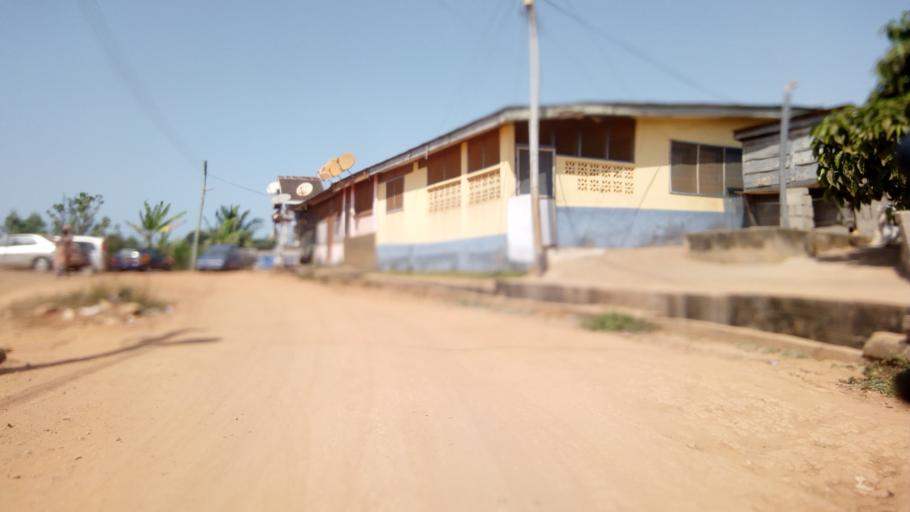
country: GH
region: Central
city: Cape Coast
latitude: 5.1125
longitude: -1.2650
